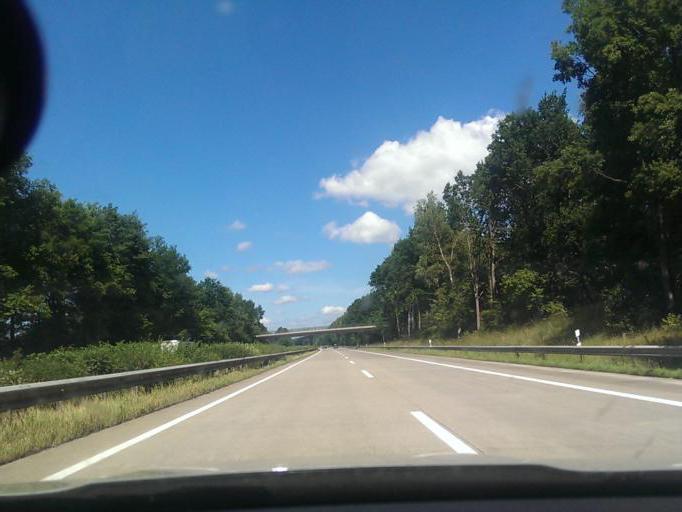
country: DE
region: Lower Saxony
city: Walsrode
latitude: 52.8606
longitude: 9.5402
